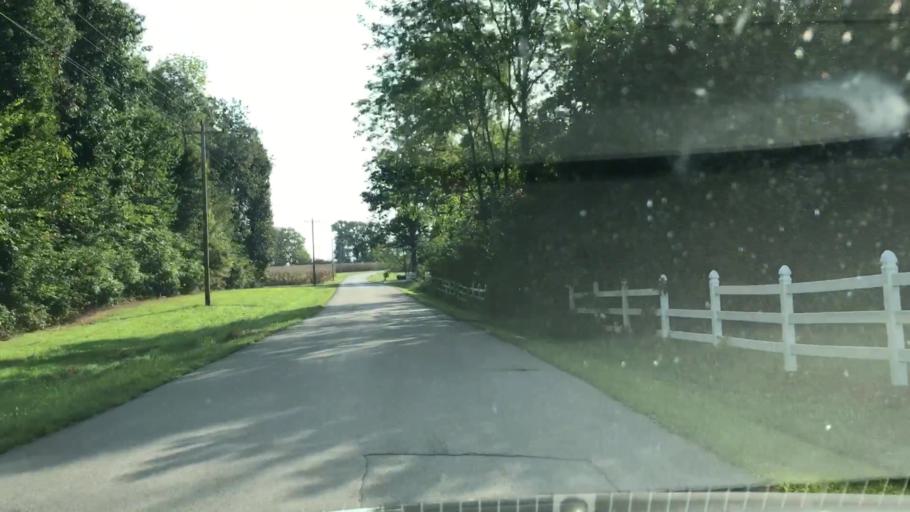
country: US
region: Kentucky
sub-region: Todd County
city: Elkton
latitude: 36.7668
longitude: -87.1617
